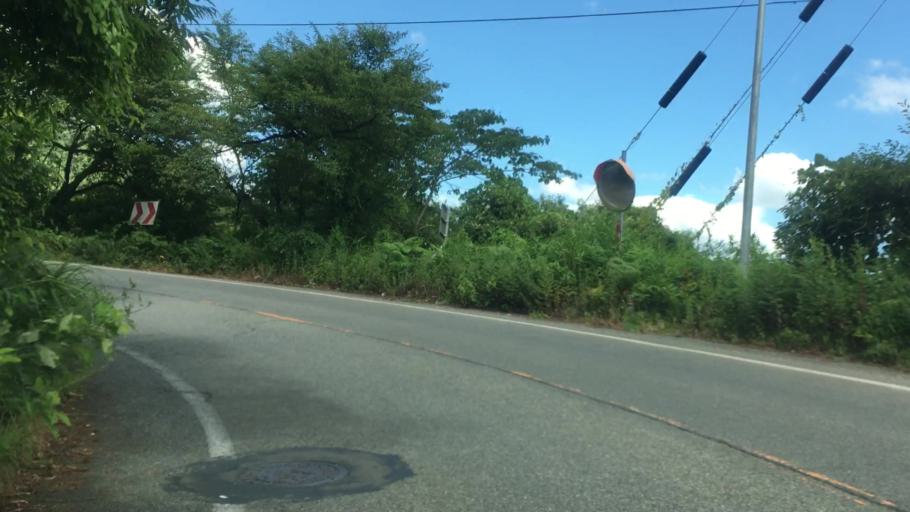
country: JP
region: Hyogo
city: Toyooka
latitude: 35.4908
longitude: 134.6894
